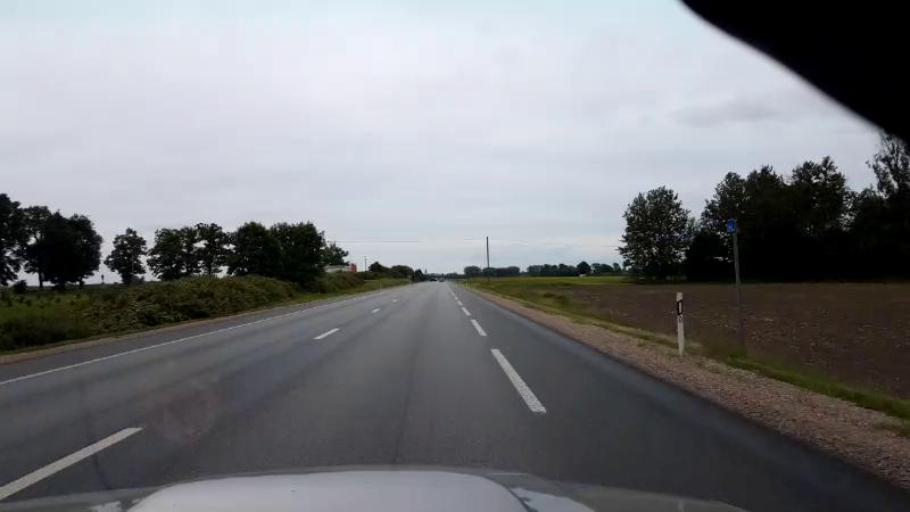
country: LV
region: Lecava
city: Iecava
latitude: 56.6187
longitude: 24.2175
